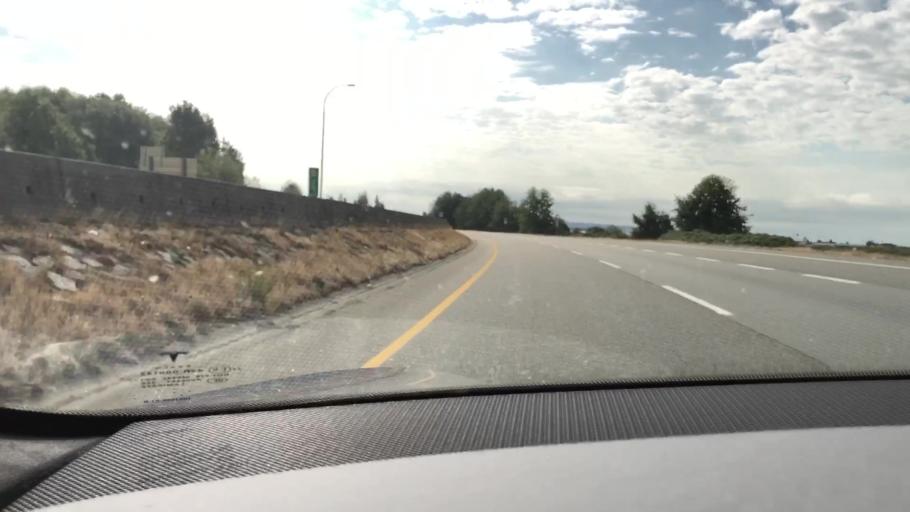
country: CA
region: British Columbia
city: Delta
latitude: 49.1184
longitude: -122.9262
